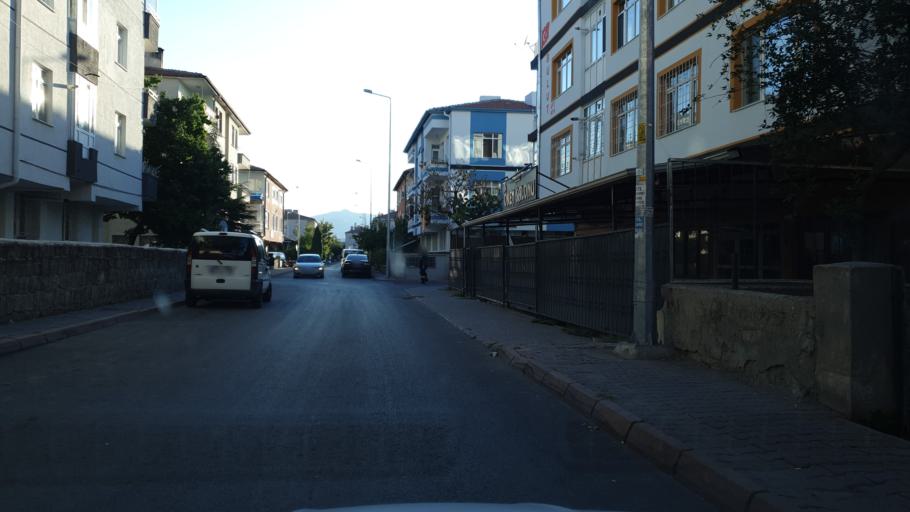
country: TR
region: Kayseri
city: Kayseri
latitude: 38.7377
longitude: 35.4913
